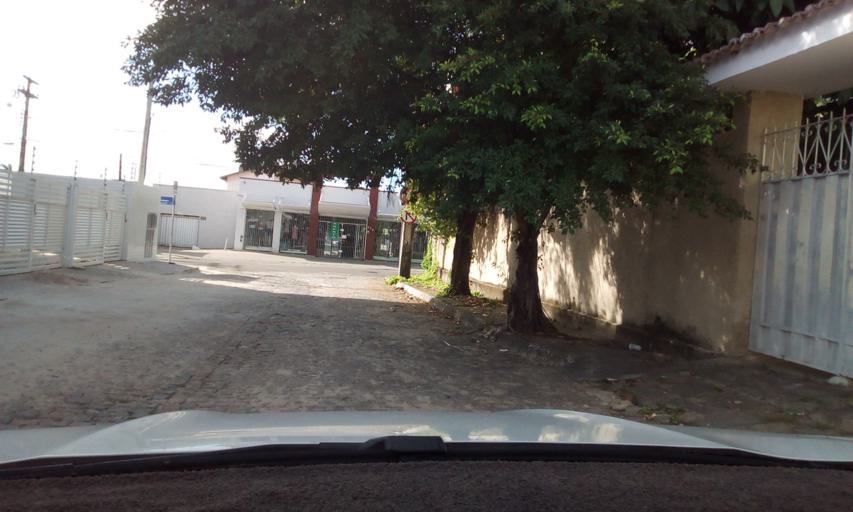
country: BR
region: Paraiba
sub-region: Joao Pessoa
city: Joao Pessoa
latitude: -7.1139
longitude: -34.8566
